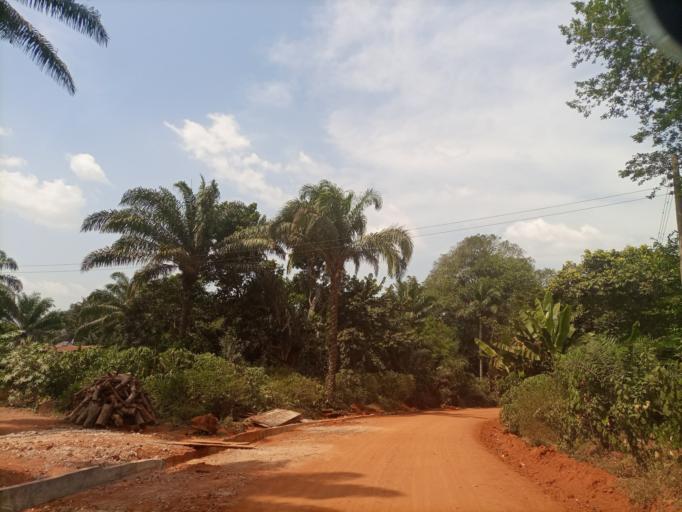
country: NG
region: Enugu
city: Obollo-Afor
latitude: 6.8652
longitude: 7.4732
